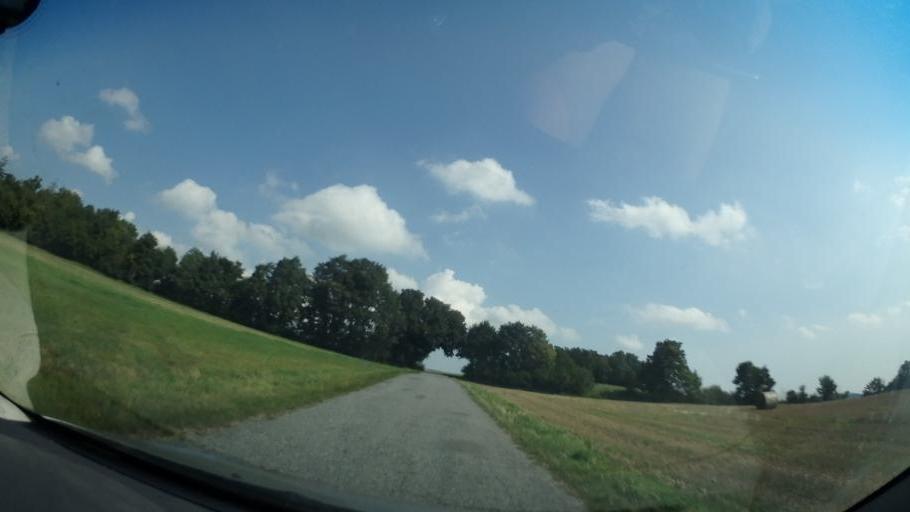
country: CZ
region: Pardubicky
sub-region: Okres Svitavy
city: Bystre
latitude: 49.5666
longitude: 16.3555
